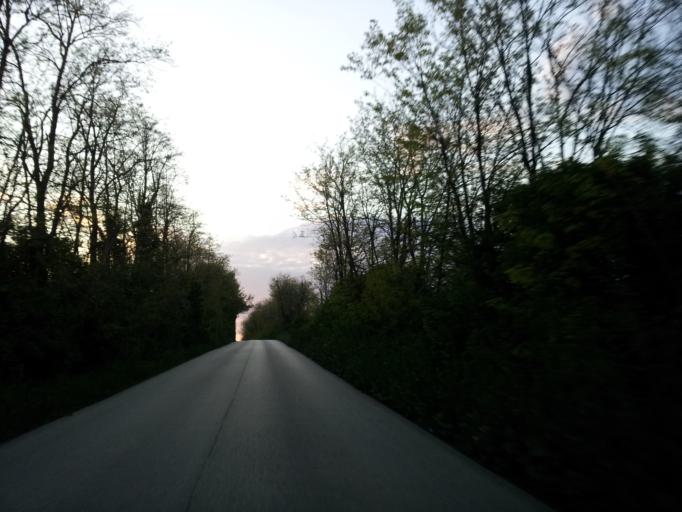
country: HU
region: Pest
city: Perbal
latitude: 47.6243
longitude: 18.7661
